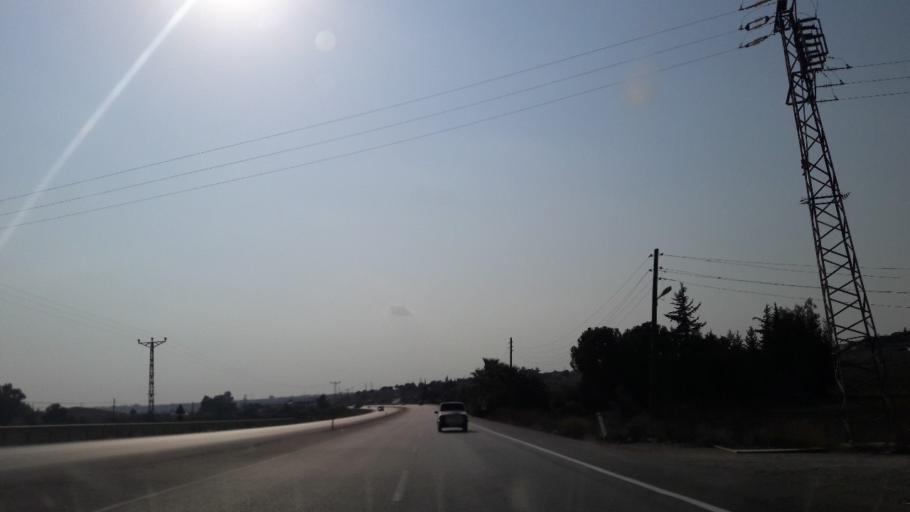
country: TR
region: Adana
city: Yuregir
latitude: 37.0740
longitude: 35.4656
